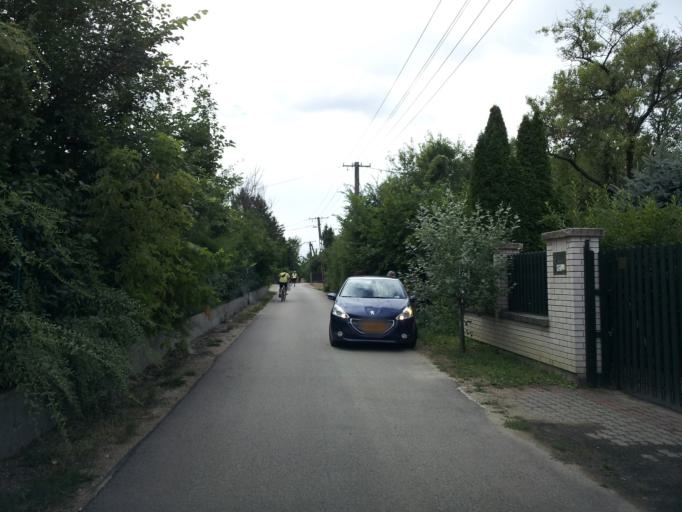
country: HU
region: Veszprem
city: Balatonkenese
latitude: 47.0091
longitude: 18.1659
